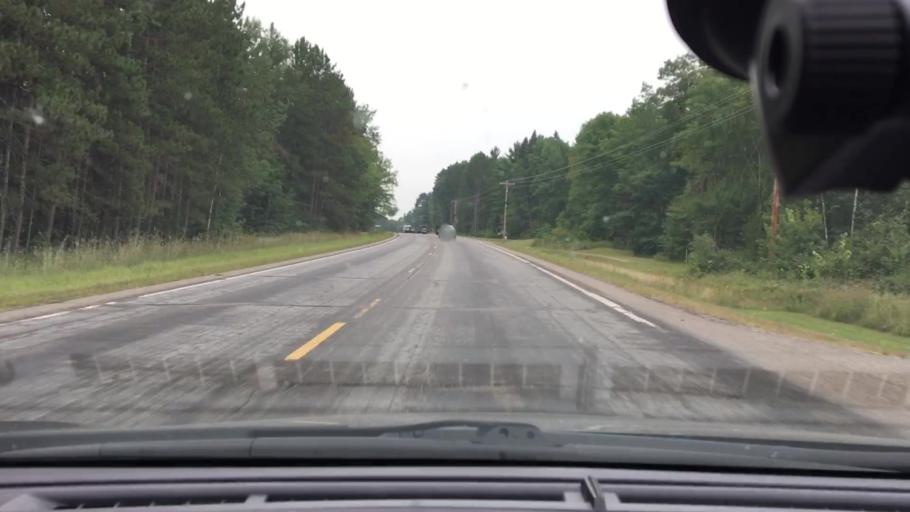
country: US
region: Minnesota
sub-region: Crow Wing County
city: Cross Lake
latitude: 46.7981
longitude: -93.9614
